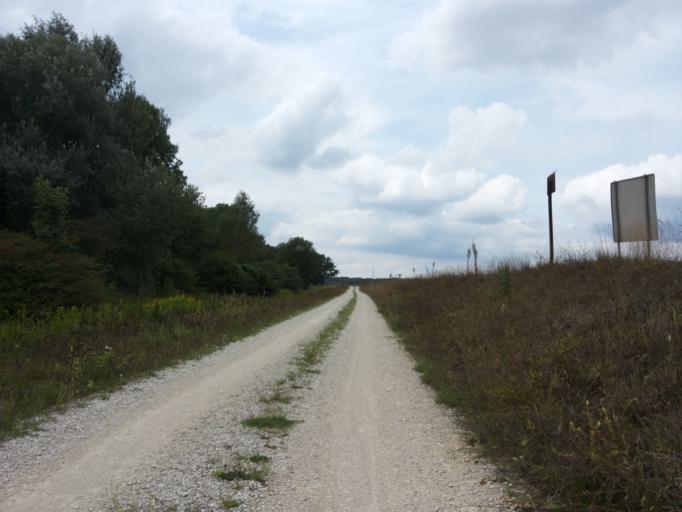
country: DE
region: Bavaria
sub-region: Upper Bavaria
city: Bergheim
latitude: 48.7499
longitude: 11.2687
